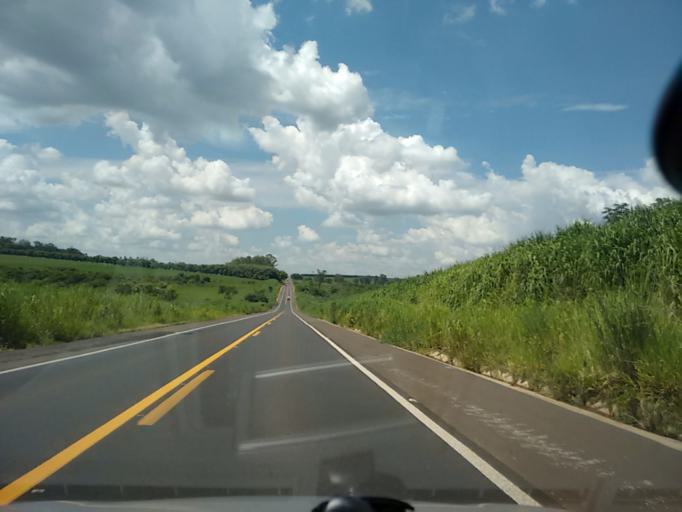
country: BR
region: Sao Paulo
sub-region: Osvaldo Cruz
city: Osvaldo Cruz
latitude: -21.8853
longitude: -50.8682
